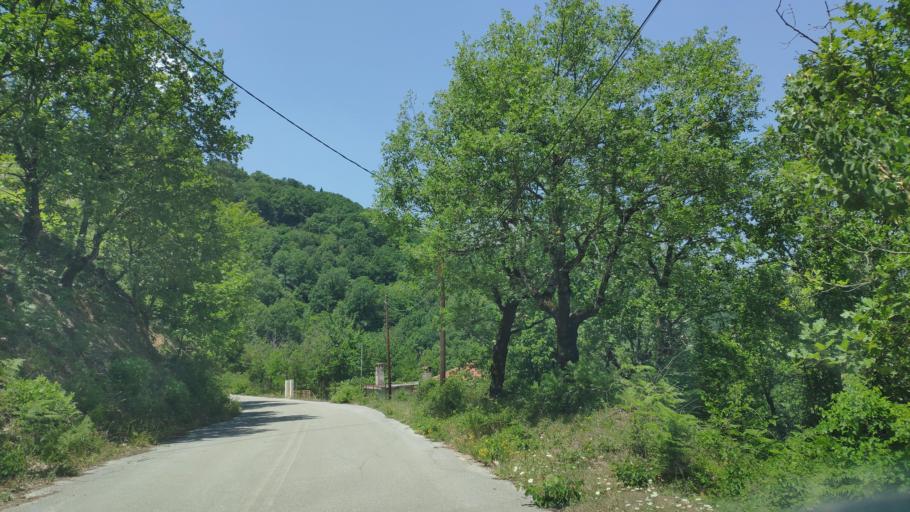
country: GR
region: Epirus
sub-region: Nomos Artas
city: Ano Kalentini
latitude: 39.1974
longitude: 21.3459
